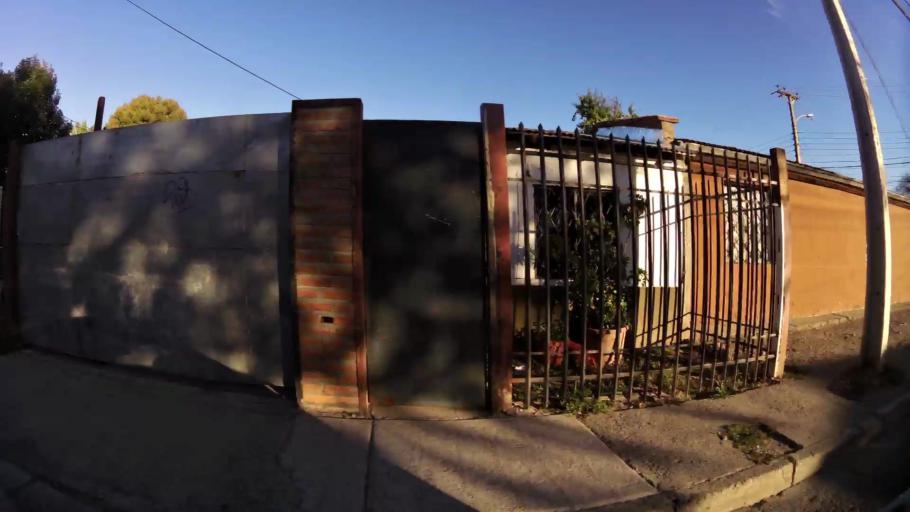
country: CL
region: O'Higgins
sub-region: Provincia de Cachapoal
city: Rancagua
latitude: -34.1730
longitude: -70.7587
